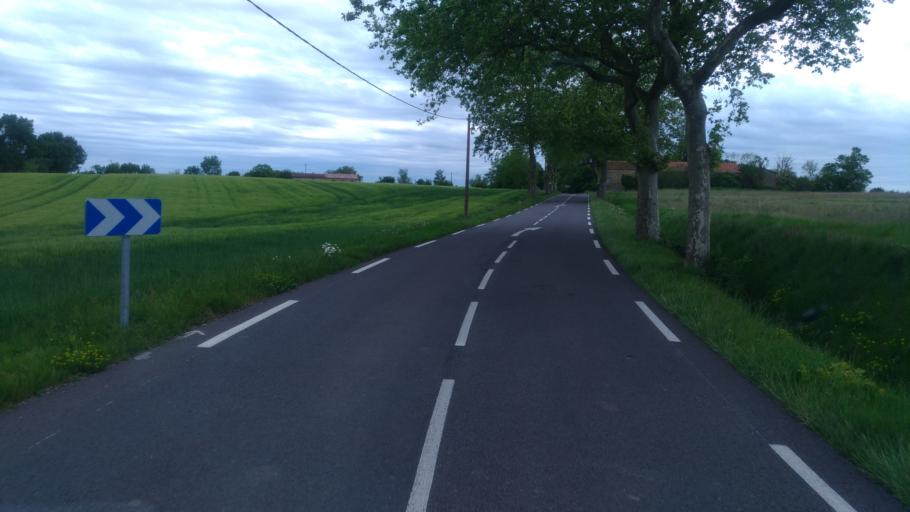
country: FR
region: Midi-Pyrenees
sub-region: Departement de la Haute-Garonne
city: Villefranche-de-Lauragais
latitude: 43.4356
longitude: 1.7772
